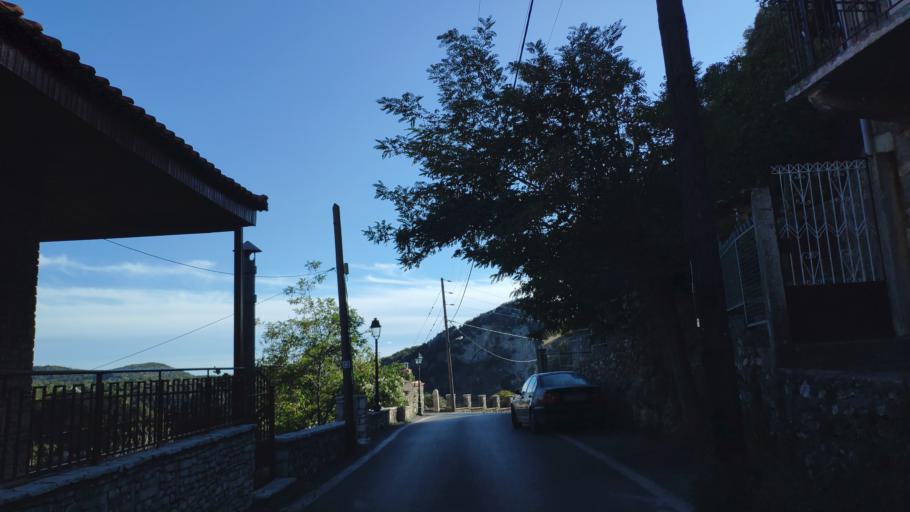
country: GR
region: Peloponnese
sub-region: Nomos Arkadias
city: Dimitsana
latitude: 37.5532
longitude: 22.0781
